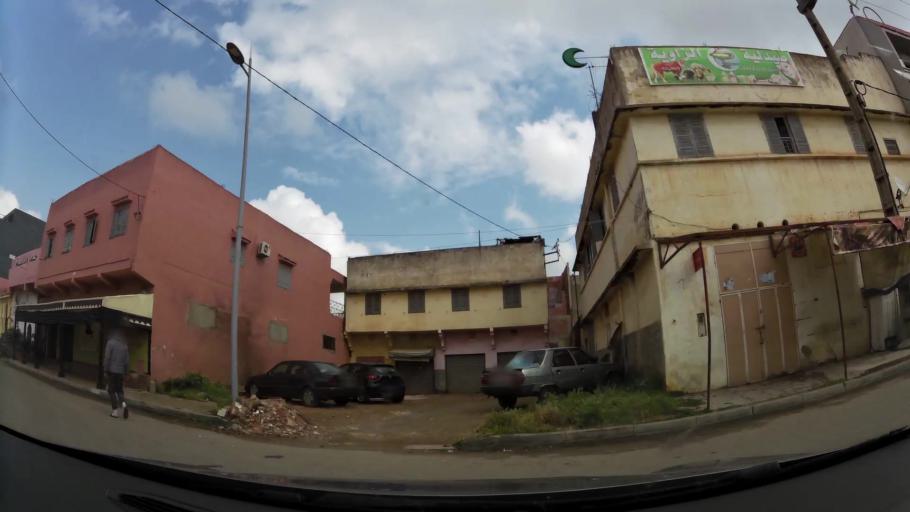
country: MA
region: Rabat-Sale-Zemmour-Zaer
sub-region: Khemisset
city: Tiflet
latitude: 33.8946
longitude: -6.3090
